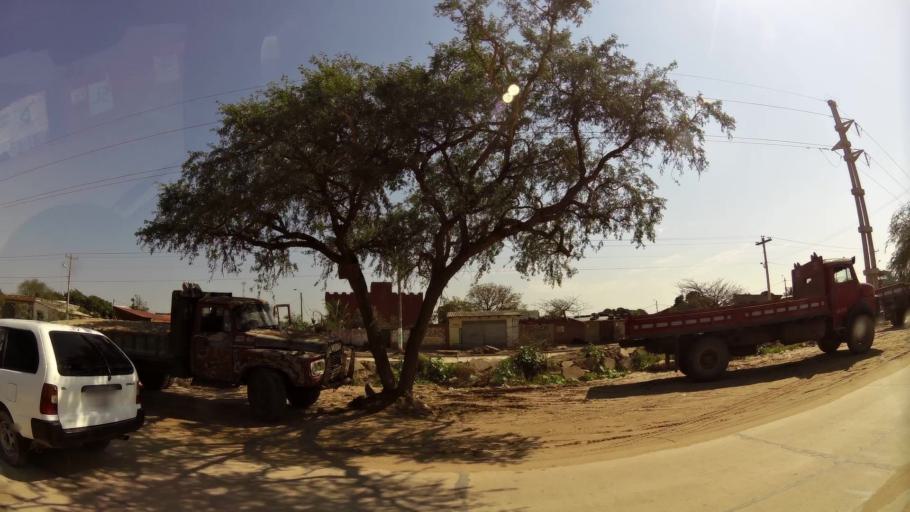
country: BO
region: Santa Cruz
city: Cotoca
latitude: -17.7500
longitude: -63.0943
